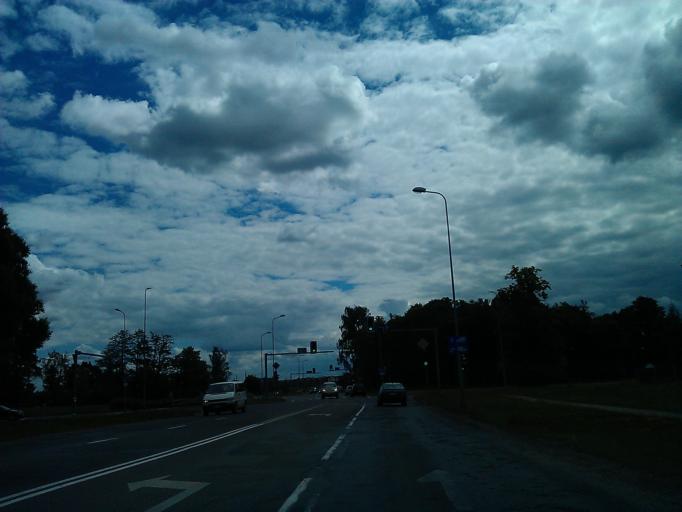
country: LV
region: Jelgava
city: Jelgava
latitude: 56.6426
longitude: 23.6952
